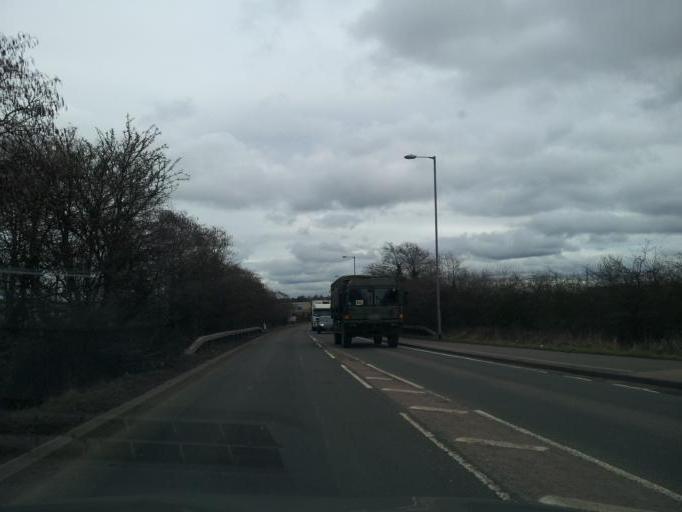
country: GB
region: England
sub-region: Staffordshire
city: Stafford
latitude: 52.8334
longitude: -2.1184
